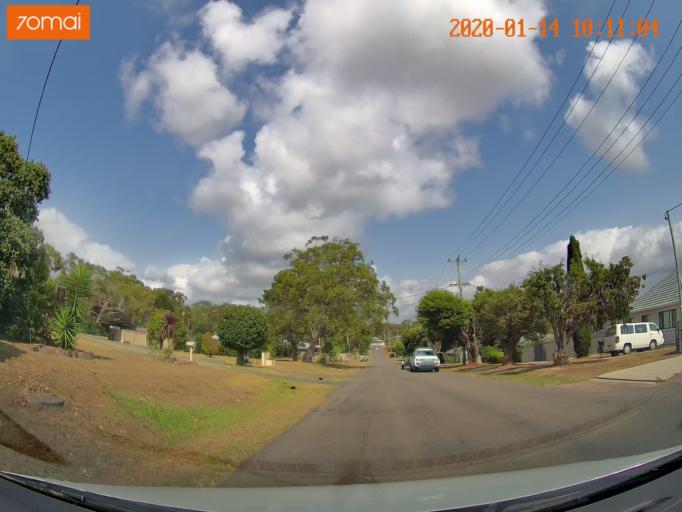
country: AU
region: New South Wales
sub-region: Wyong Shire
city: Kingfisher Shores
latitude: -33.1202
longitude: 151.5340
